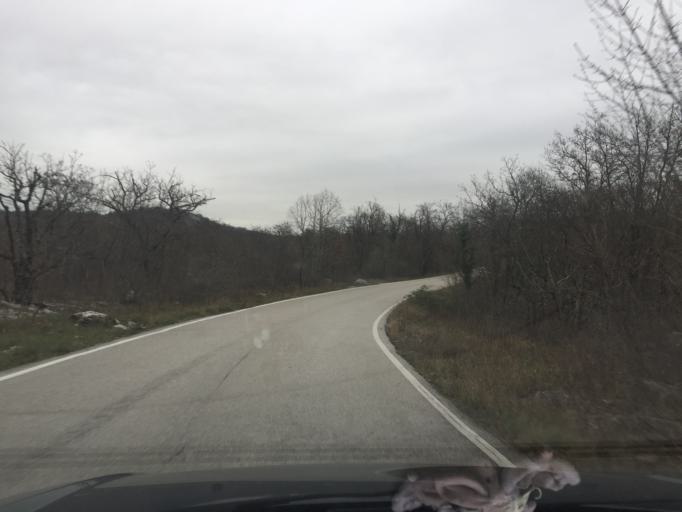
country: IT
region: Friuli Venezia Giulia
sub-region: Provincia di Trieste
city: Zolla
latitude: 45.7091
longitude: 13.8152
